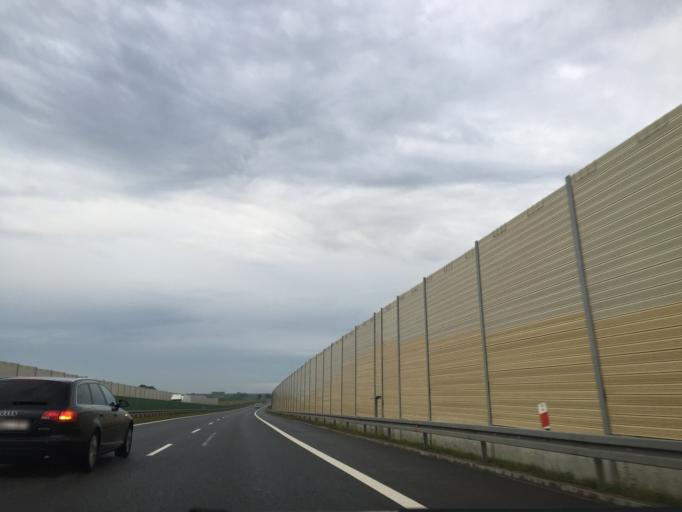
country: PL
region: Podlasie
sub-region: Powiat zambrowski
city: Zambrow
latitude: 52.9995
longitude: 22.2502
